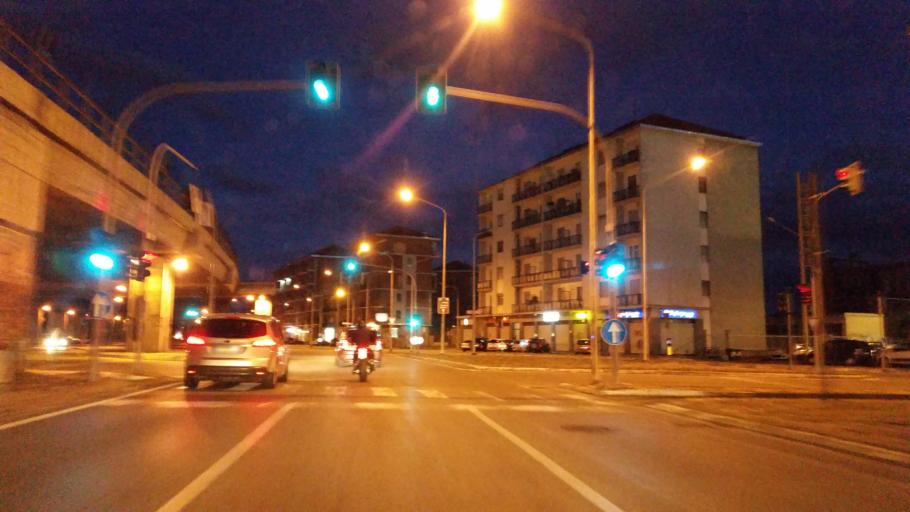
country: IT
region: Piedmont
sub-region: Provincia di Torino
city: Moncalieri
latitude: 45.0053
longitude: 7.6730
